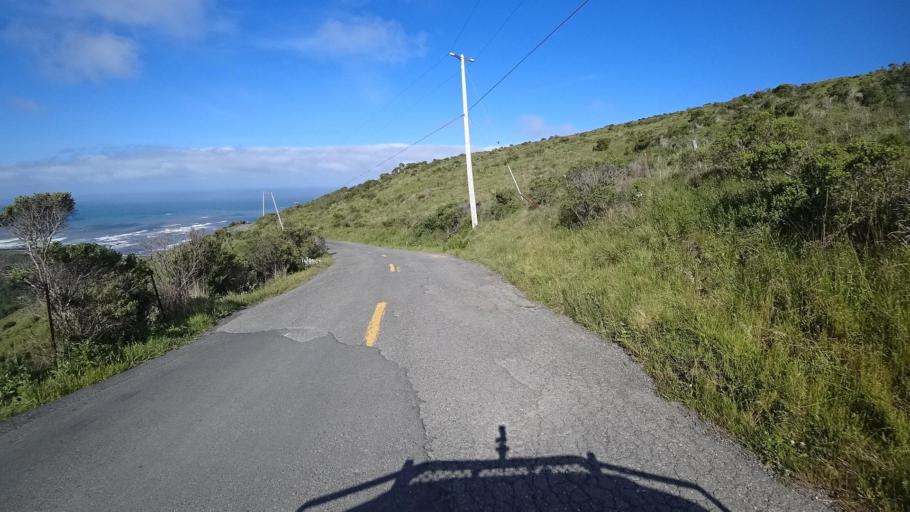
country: US
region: California
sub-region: Humboldt County
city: Ferndale
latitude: 40.4363
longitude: -124.3934
